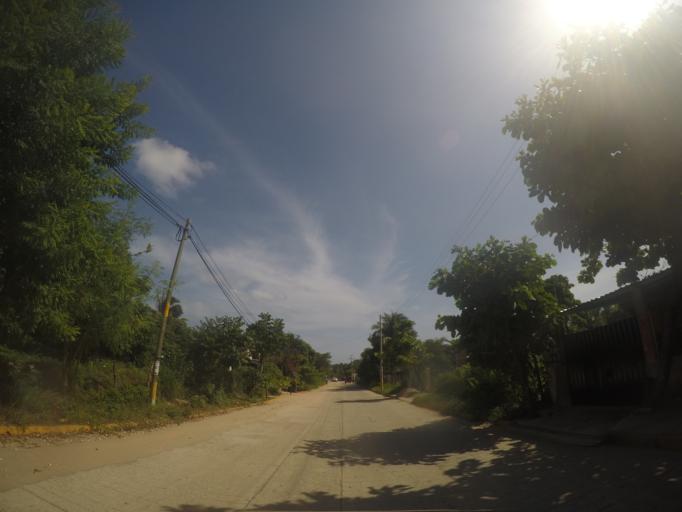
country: MX
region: Oaxaca
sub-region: Santa Maria Colotepec
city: Brisas de Zicatela
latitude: 15.8392
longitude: -97.0440
